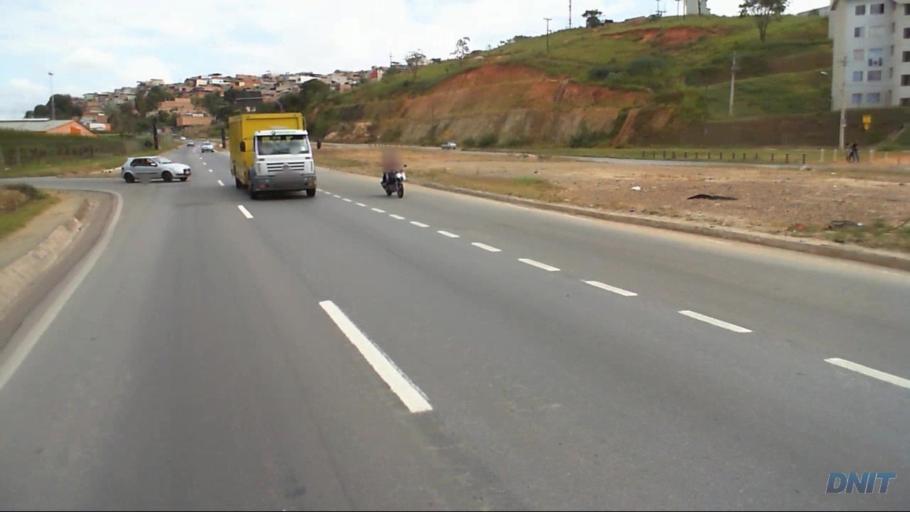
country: BR
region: Minas Gerais
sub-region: Santa Luzia
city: Santa Luzia
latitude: -19.8448
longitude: -43.8864
